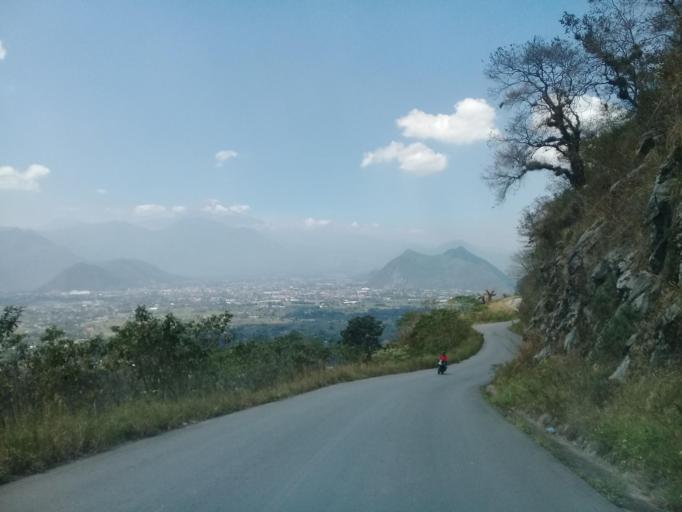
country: MX
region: Veracruz
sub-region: Tlilapan
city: Tonalixco
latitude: 18.8038
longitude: -97.0596
